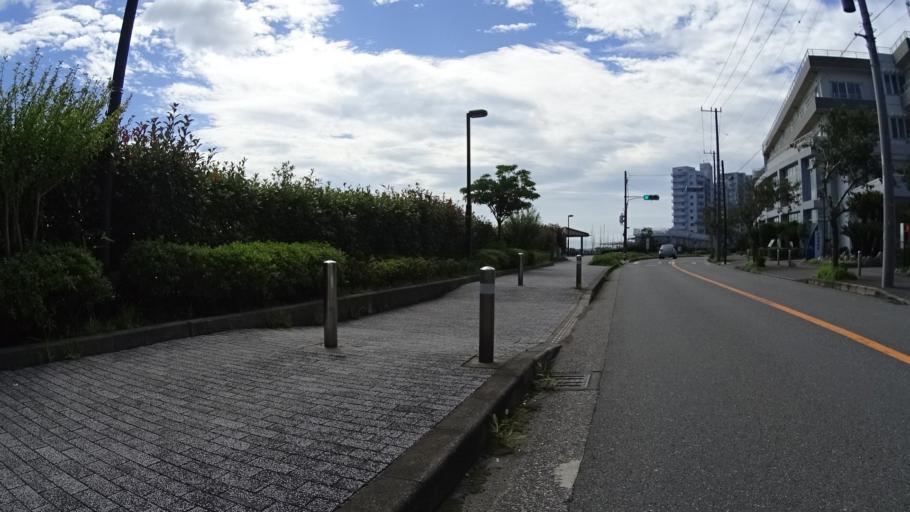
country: JP
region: Kanagawa
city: Yokosuka
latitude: 35.2395
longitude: 139.7207
